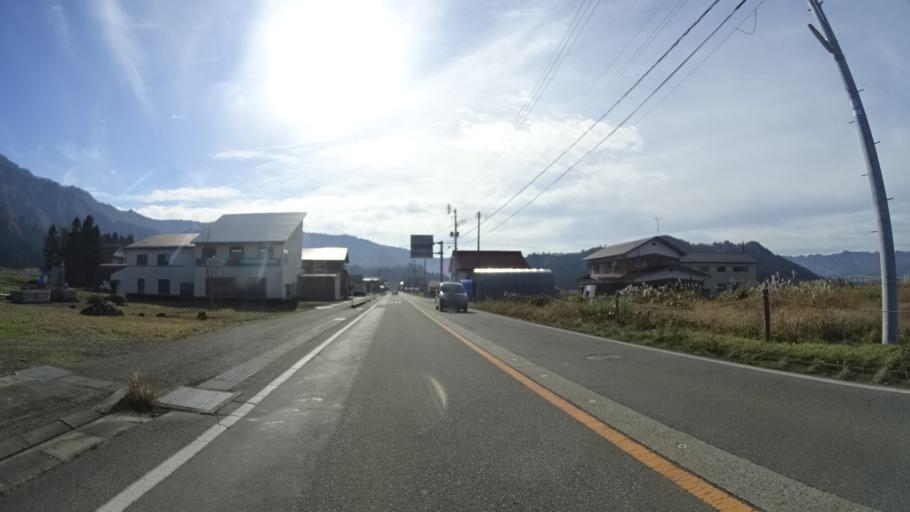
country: JP
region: Niigata
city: Muikamachi
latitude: 37.1457
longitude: 138.9598
